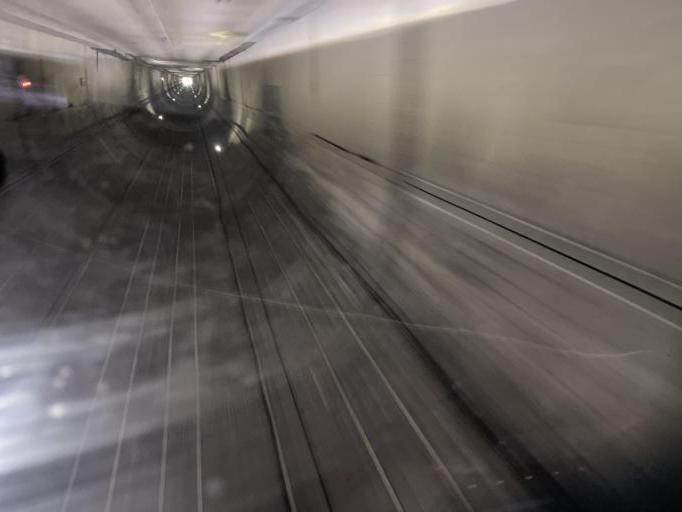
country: JP
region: Nagano
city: Omachi
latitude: 36.4931
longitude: 137.7340
